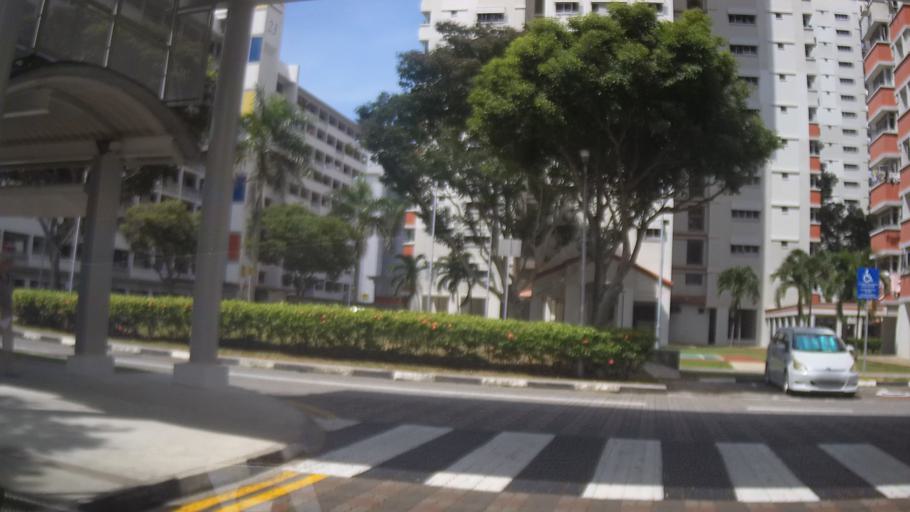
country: SG
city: Singapore
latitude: 1.3306
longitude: 103.8860
